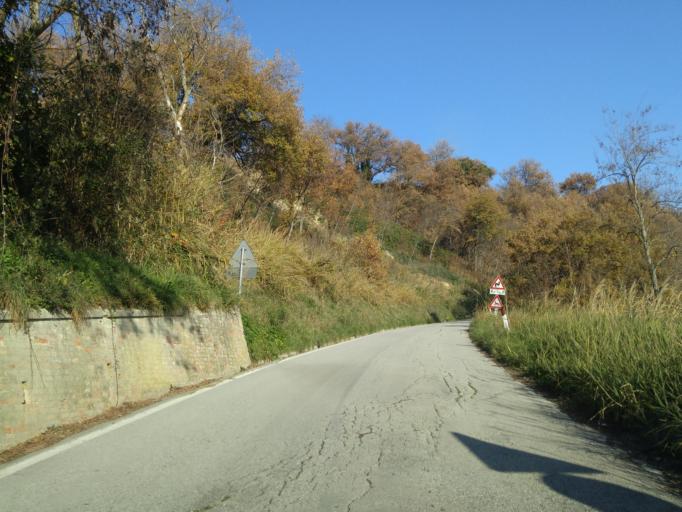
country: IT
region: The Marches
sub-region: Provincia di Pesaro e Urbino
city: Isola del Piano
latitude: 43.7557
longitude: 12.7991
